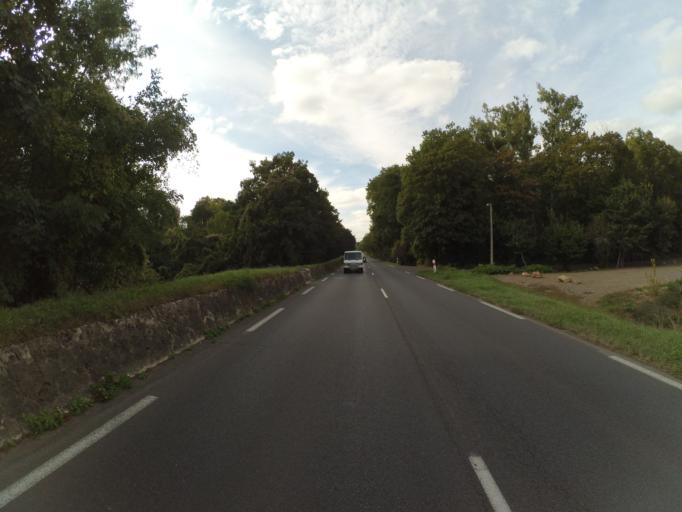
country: FR
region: Centre
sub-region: Departement d'Indre-et-Loire
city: Vouvray
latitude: 47.4103
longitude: 0.7851
